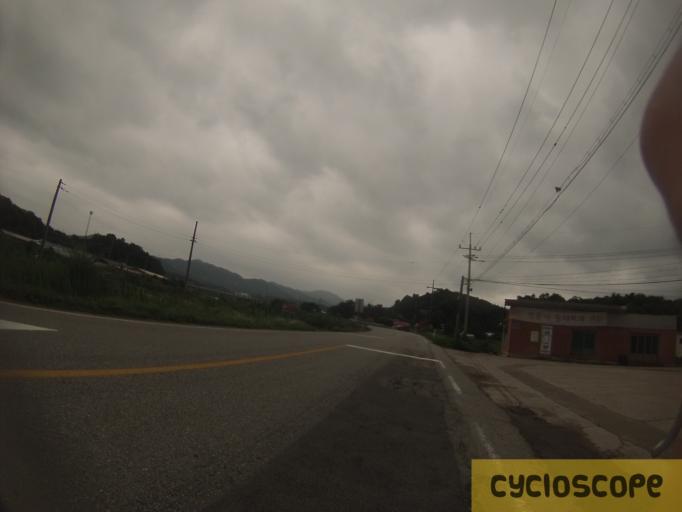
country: KR
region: Chungcheongnam-do
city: Yesan
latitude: 36.6080
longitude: 126.7921
